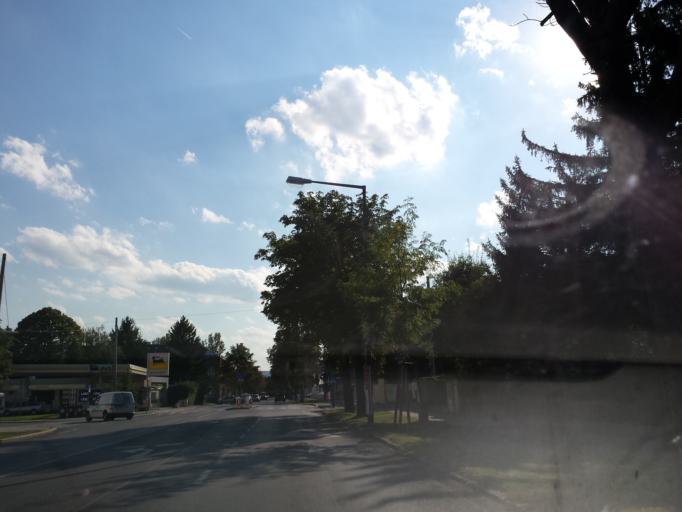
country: AT
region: Lower Austria
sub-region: Politischer Bezirk Modling
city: Vosendorf
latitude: 48.1575
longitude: 16.3058
